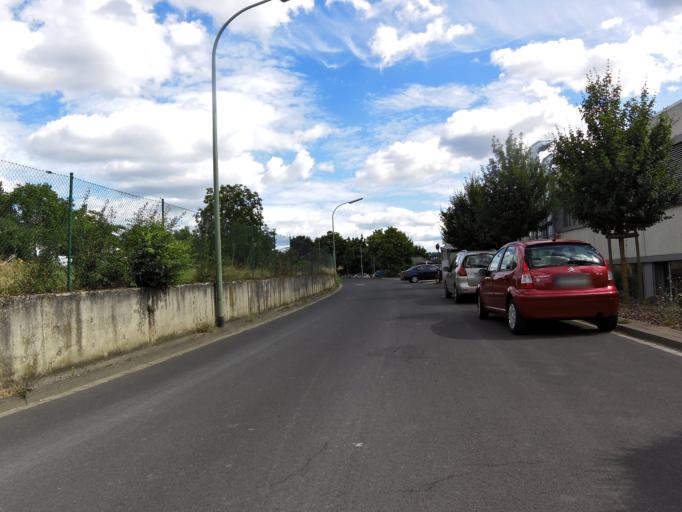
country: DE
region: Bavaria
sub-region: Regierungsbezirk Unterfranken
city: Zell am Main
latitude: 49.8084
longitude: 9.8901
